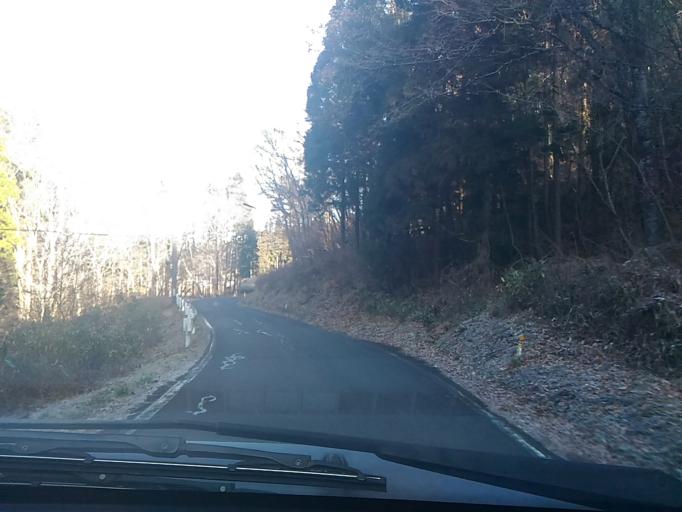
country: JP
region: Fukushima
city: Ishikawa
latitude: 37.0004
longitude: 140.5443
